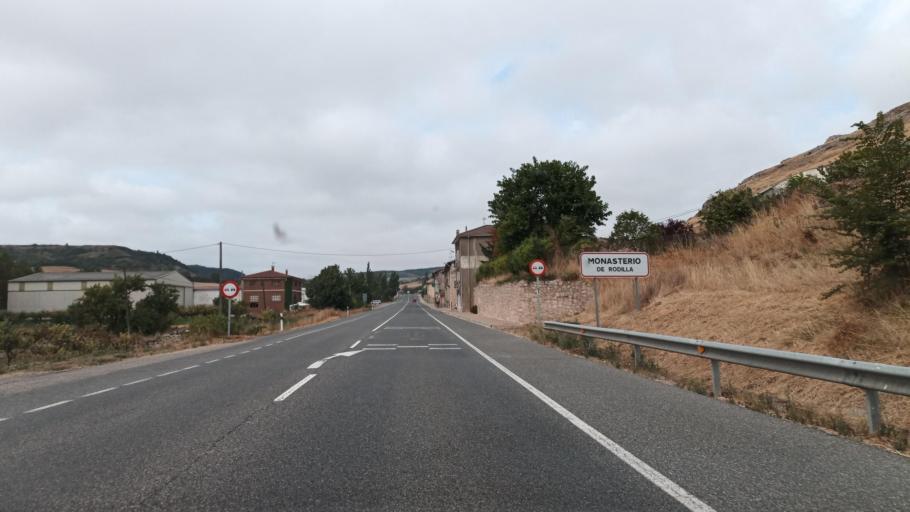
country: ES
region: Castille and Leon
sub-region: Provincia de Burgos
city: Monasterio de Rodilla
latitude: 42.4585
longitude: -3.4639
